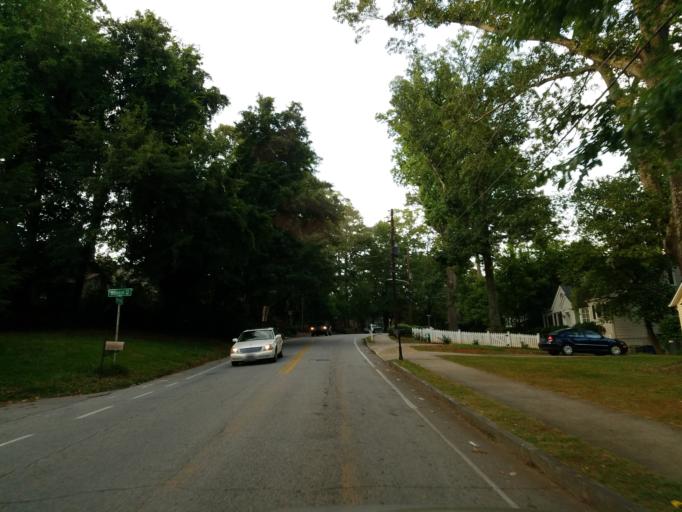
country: US
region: Georgia
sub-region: DeKalb County
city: North Atlanta
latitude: 33.8517
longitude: -84.3855
